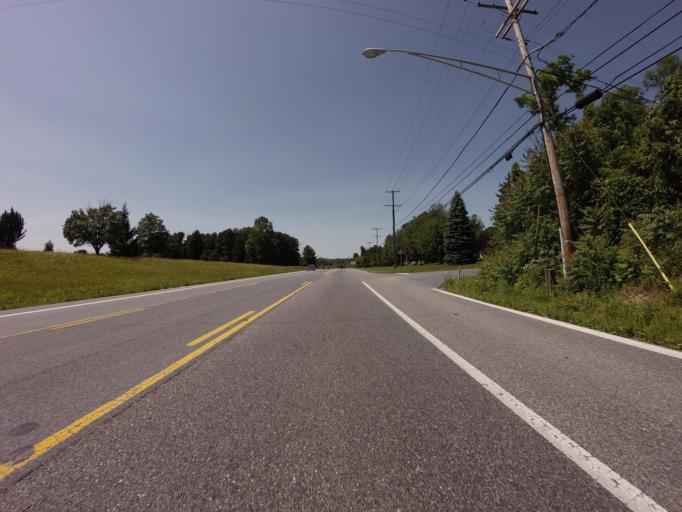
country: US
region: Maryland
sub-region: Carroll County
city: Sykesville
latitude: 39.3377
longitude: -76.9529
